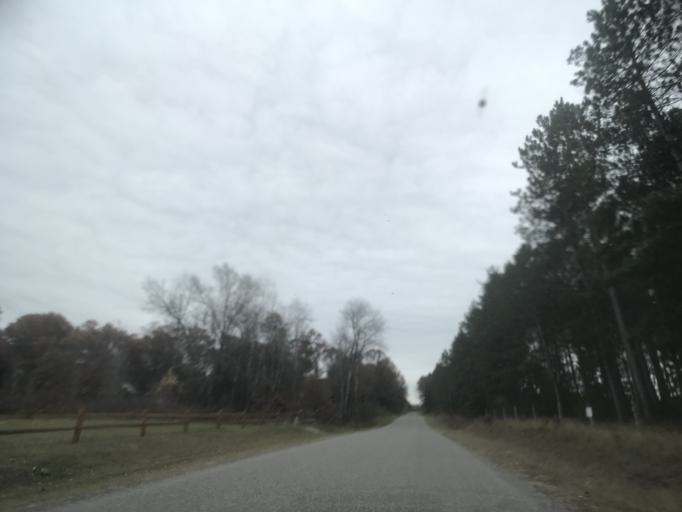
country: US
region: Wisconsin
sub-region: Oconto County
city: Gillett
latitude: 45.3434
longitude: -88.2861
